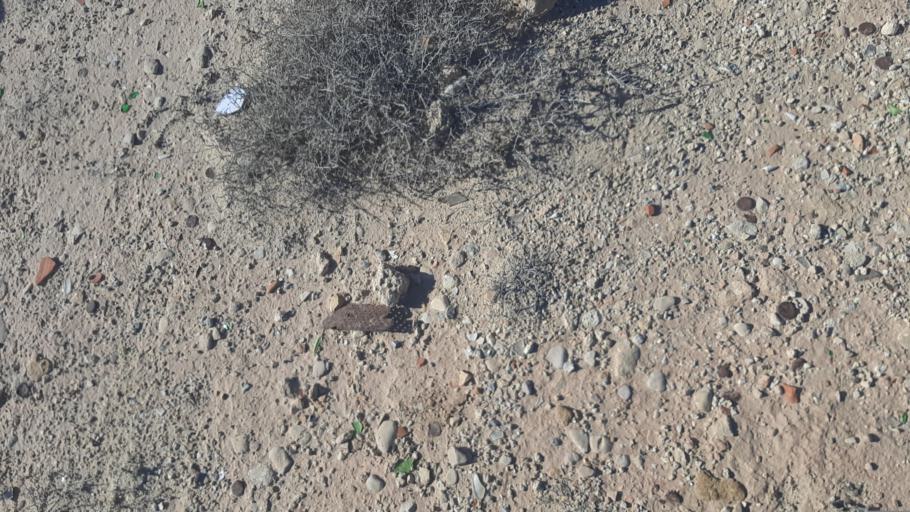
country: TN
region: Qabis
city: Gabes
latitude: 33.8672
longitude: 10.1349
